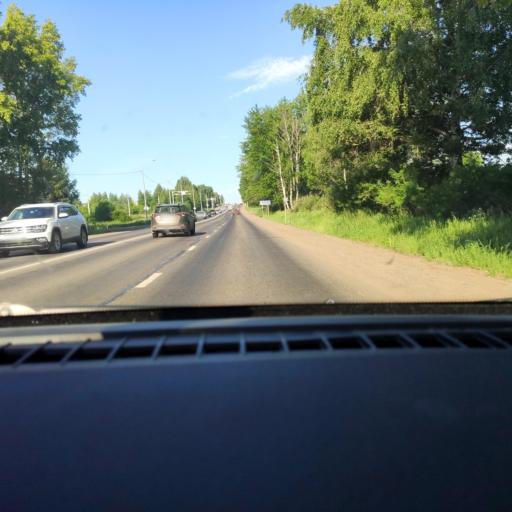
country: RU
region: Udmurtiya
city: Khokhryaki
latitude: 56.9105
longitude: 53.3708
